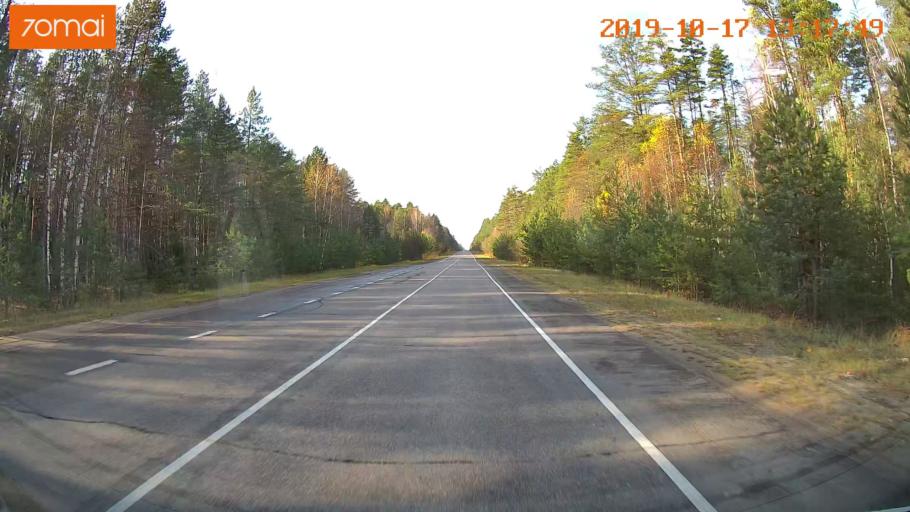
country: RU
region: Rjazan
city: Gus'-Zheleznyy
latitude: 55.0590
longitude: 41.1124
